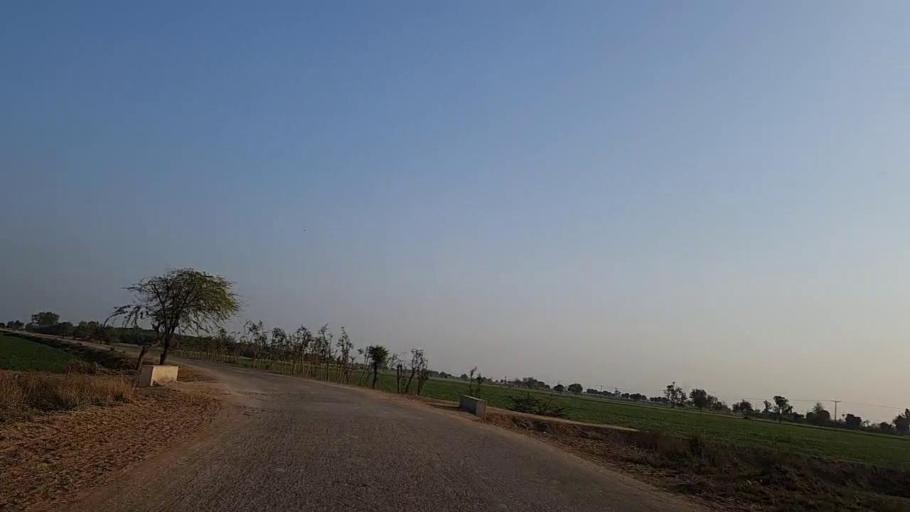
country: PK
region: Sindh
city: Sakrand
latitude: 26.0522
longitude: 68.4150
